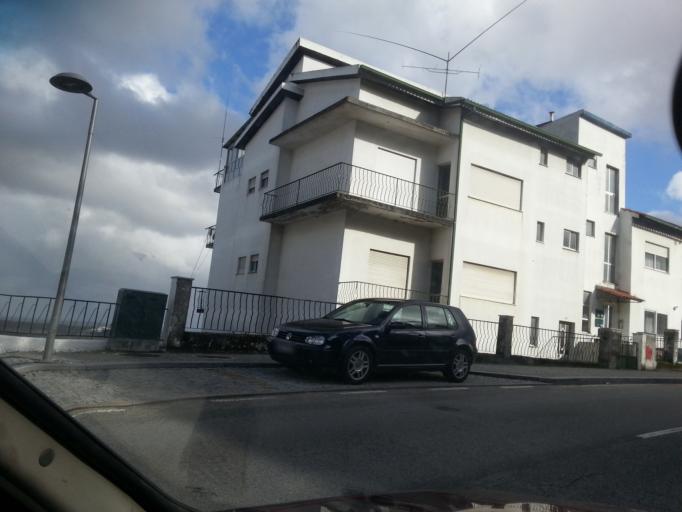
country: PT
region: Guarda
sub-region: Guarda
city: Guarda
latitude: 40.5375
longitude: -7.2615
